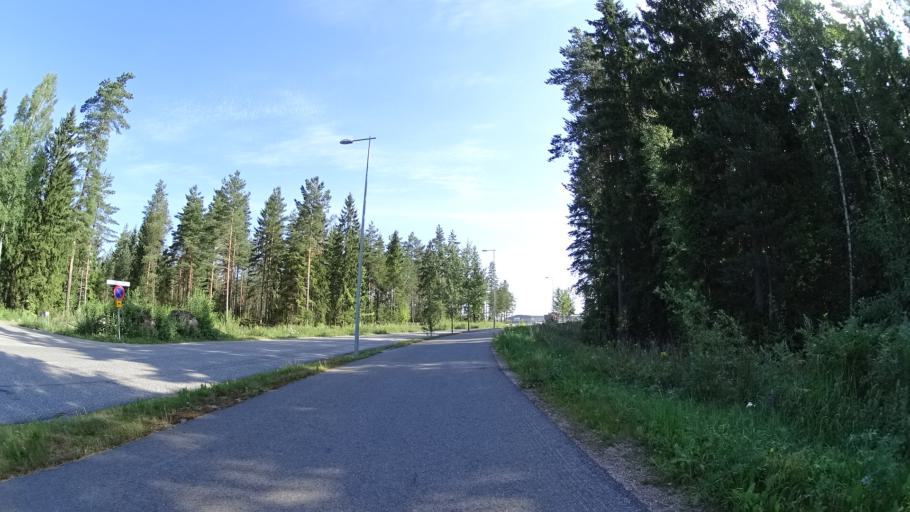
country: FI
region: Uusimaa
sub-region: Helsinki
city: Kilo
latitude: 60.2873
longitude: 24.7623
